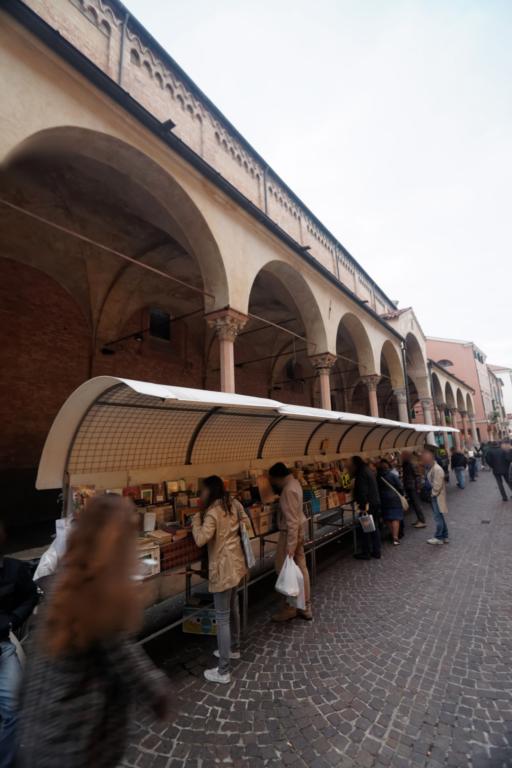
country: IT
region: Veneto
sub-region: Provincia di Padova
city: Padova
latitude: 45.4043
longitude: 11.8759
